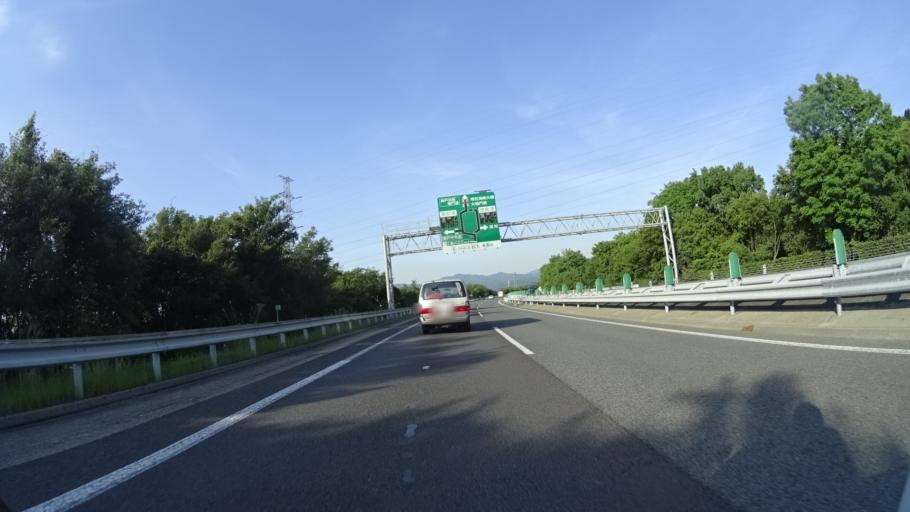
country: JP
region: Ehime
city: Kawanoecho
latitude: 33.9742
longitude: 133.5588
